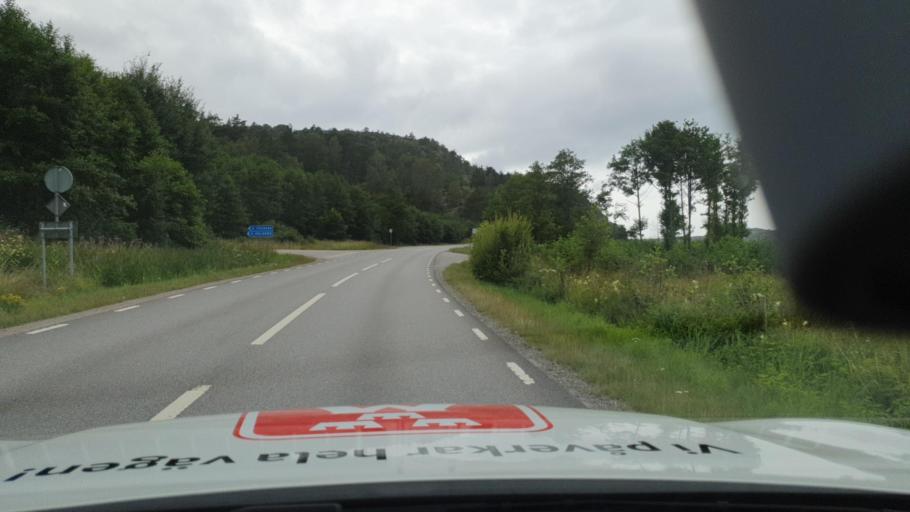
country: SE
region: Vaestra Goetaland
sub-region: Sotenas Kommun
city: Hunnebostrand
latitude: 58.4856
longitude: 11.3570
